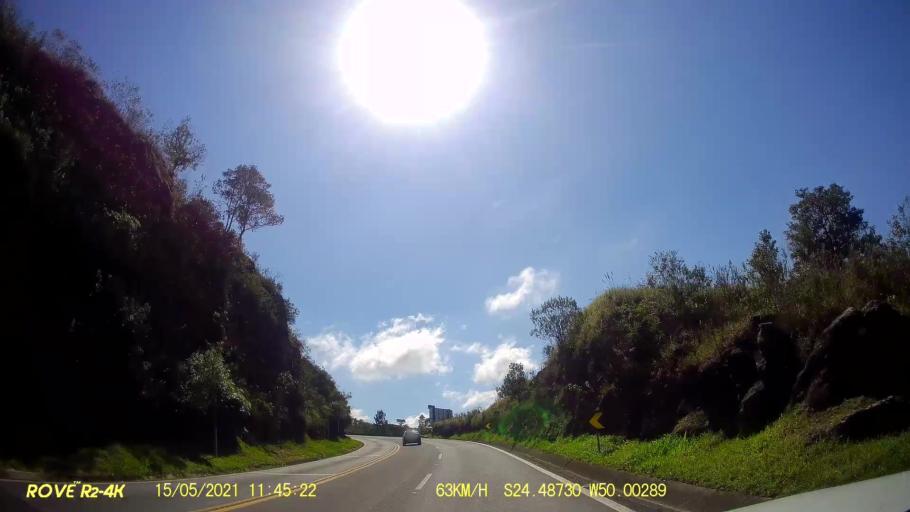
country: BR
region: Parana
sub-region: Pirai Do Sul
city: Pirai do Sul
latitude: -24.4872
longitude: -50.0025
